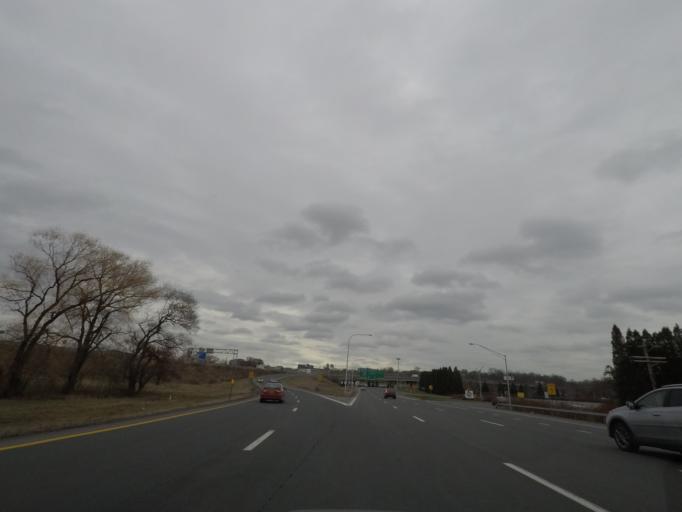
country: US
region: New York
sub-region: Schenectady County
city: Schenectady
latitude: 42.8127
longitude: -73.9546
